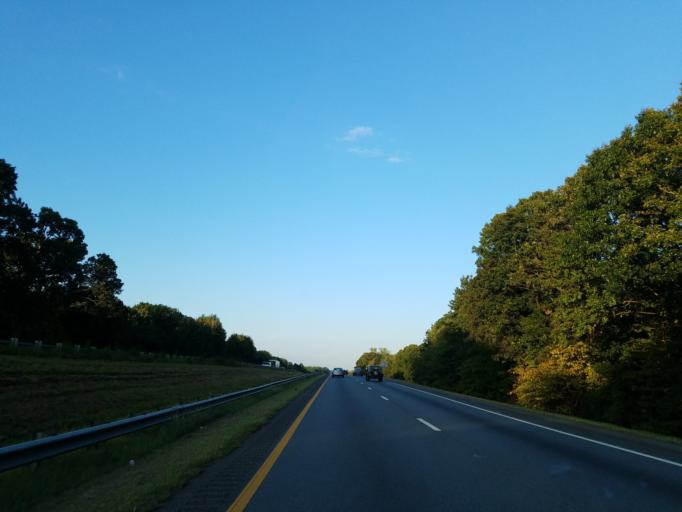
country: US
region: North Carolina
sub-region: Cleveland County
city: Kings Mountain
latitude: 35.2049
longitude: -81.3609
